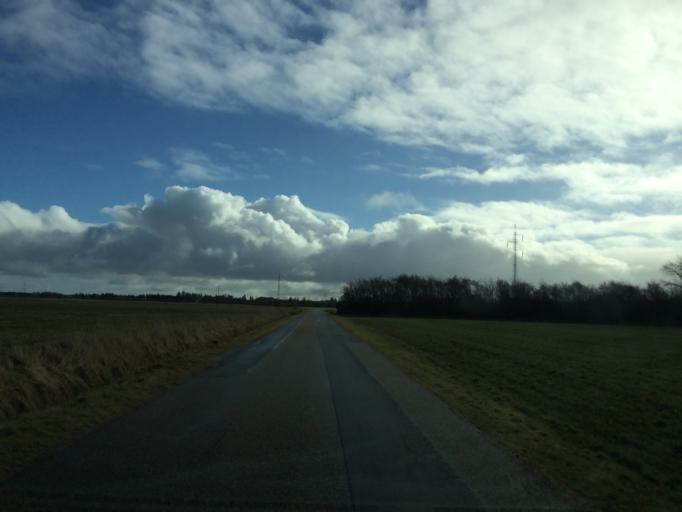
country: DK
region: Central Jutland
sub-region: Holstebro Kommune
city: Ulfborg
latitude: 56.2818
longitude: 8.3332
